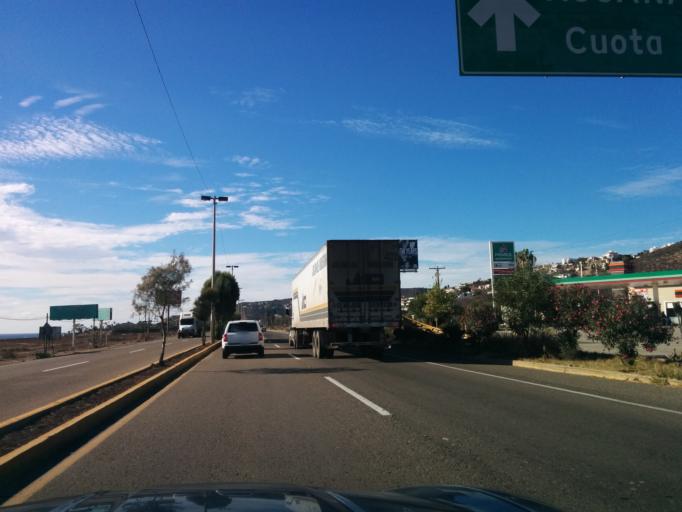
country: MX
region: Baja California
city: El Sauzal
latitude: 31.9024
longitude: -116.7159
